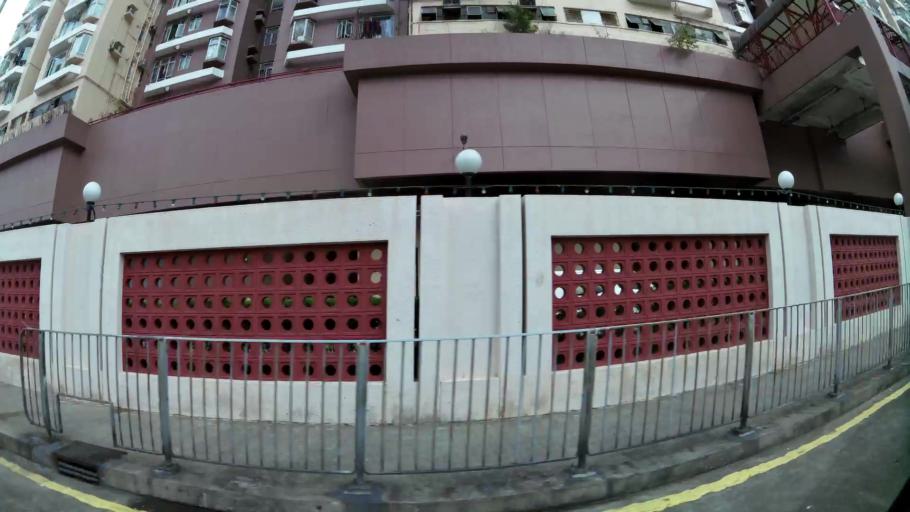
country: HK
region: Sha Tin
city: Sha Tin
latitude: 22.3980
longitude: 114.2001
